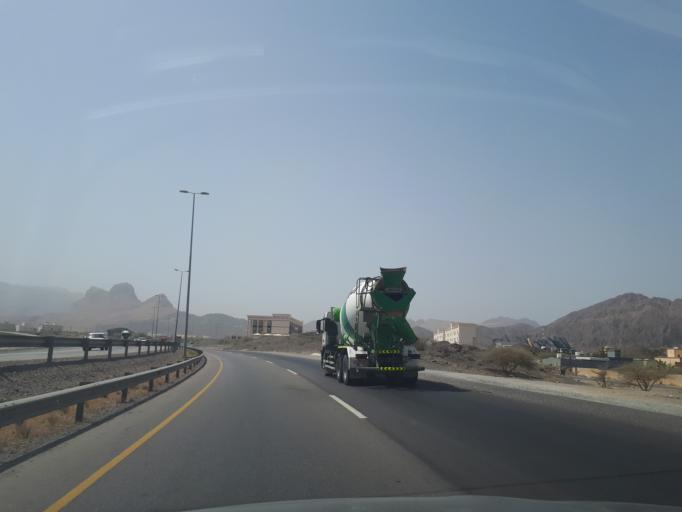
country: OM
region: Muhafazat ad Dakhiliyah
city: Bidbid
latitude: 23.5007
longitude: 58.1948
